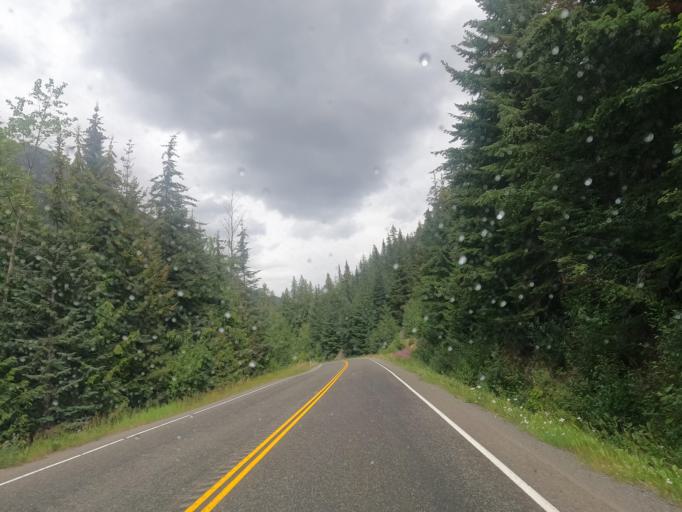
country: CA
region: British Columbia
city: Lillooet
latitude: 50.4703
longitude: -122.2344
